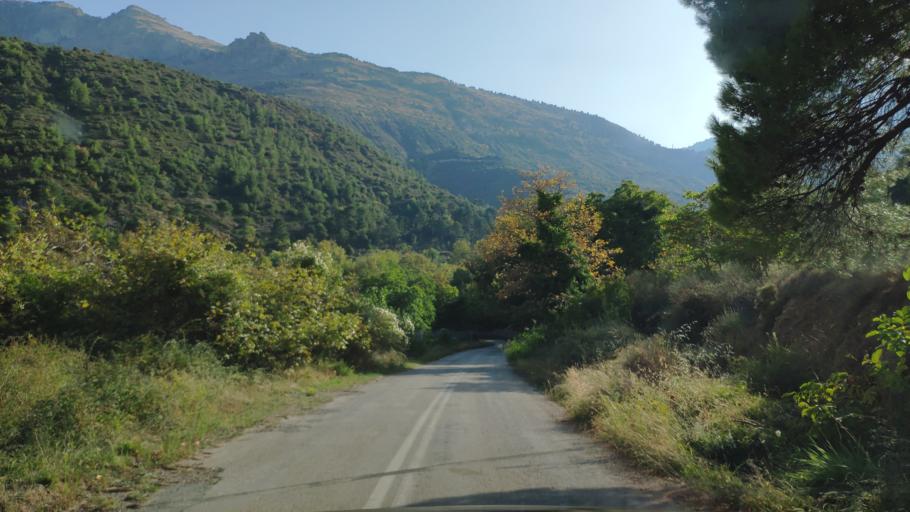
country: GR
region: West Greece
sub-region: Nomos Achaias
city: Aiyira
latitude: 38.0691
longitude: 22.3925
